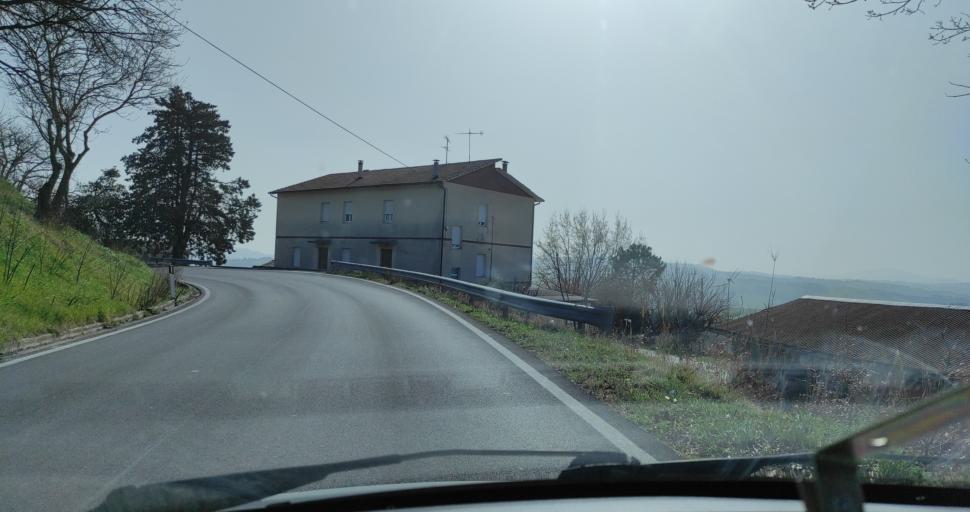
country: IT
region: The Marches
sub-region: Province of Fermo
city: Massa Fermana
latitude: 43.1786
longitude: 13.4507
